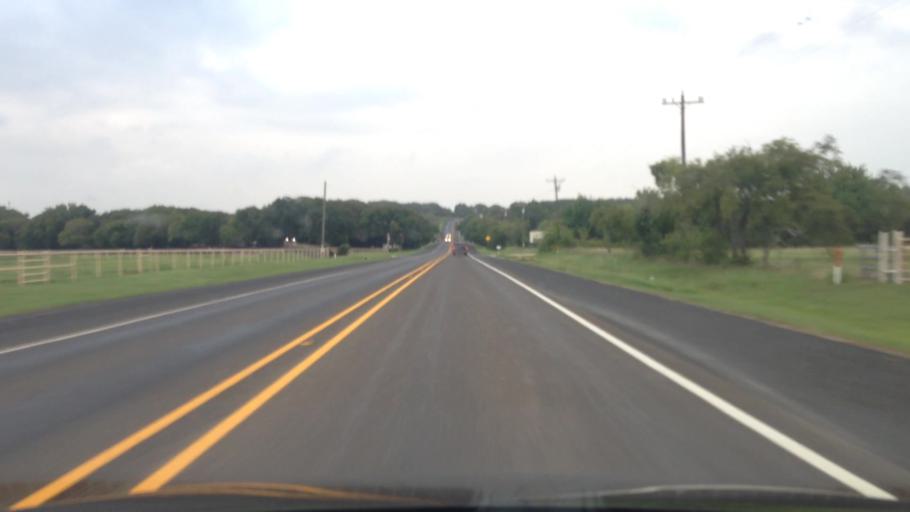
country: US
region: Texas
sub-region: Johnson County
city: Burleson
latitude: 32.5023
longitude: -97.3427
